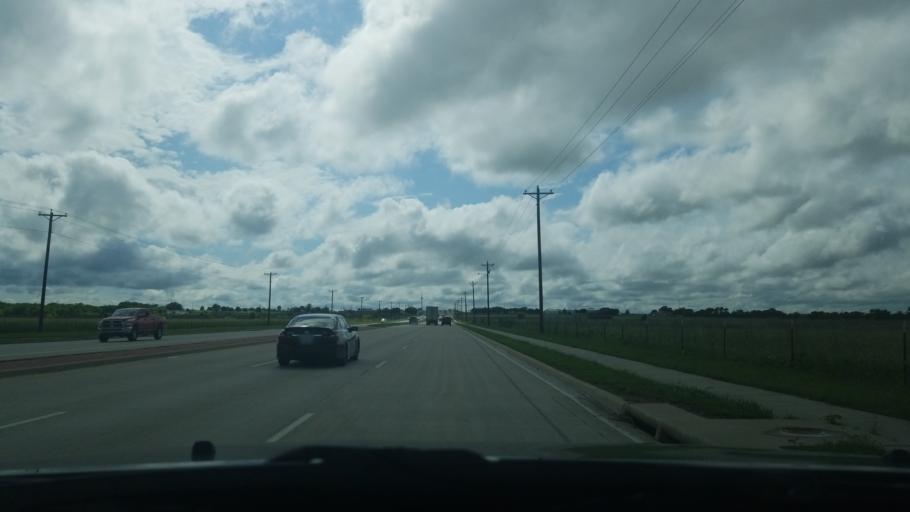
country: US
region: Texas
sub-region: Denton County
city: Krum
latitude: 33.2332
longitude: -97.2345
